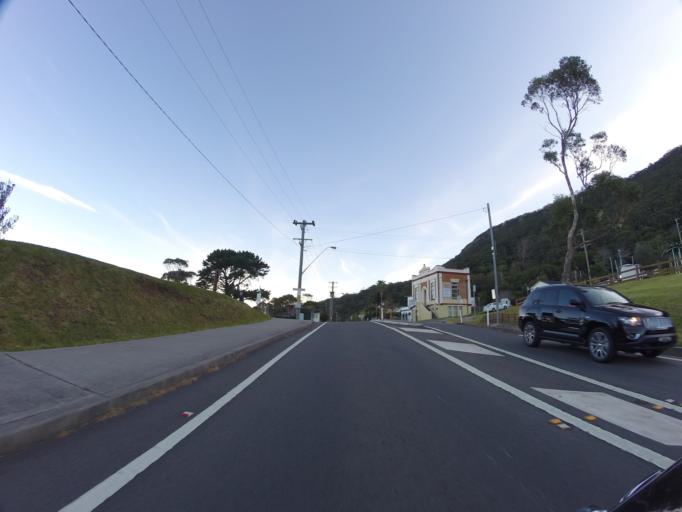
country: AU
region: New South Wales
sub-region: Wollongong
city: Helensburgh
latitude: -34.2596
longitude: 150.9697
